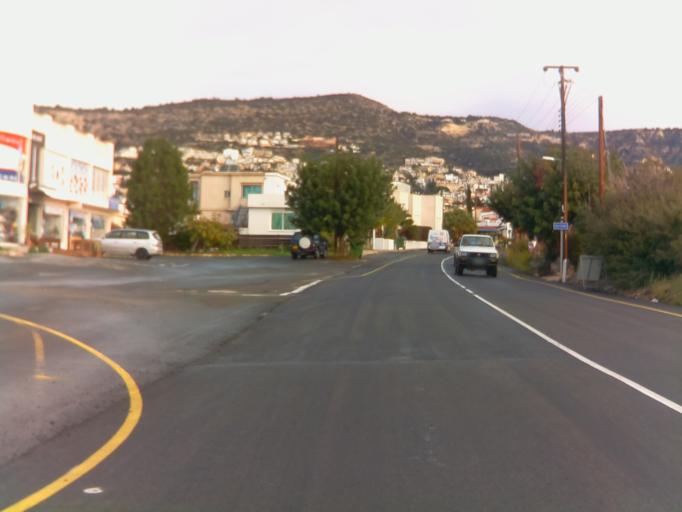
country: CY
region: Pafos
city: Pegeia
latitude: 34.8727
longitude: 32.3783
